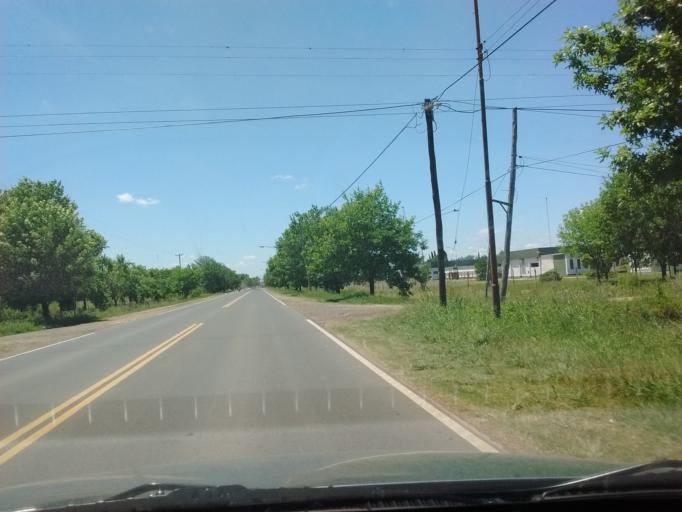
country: AR
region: Entre Rios
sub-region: Departamento de Gualeguay
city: Gualeguay
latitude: -33.1253
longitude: -59.3284
